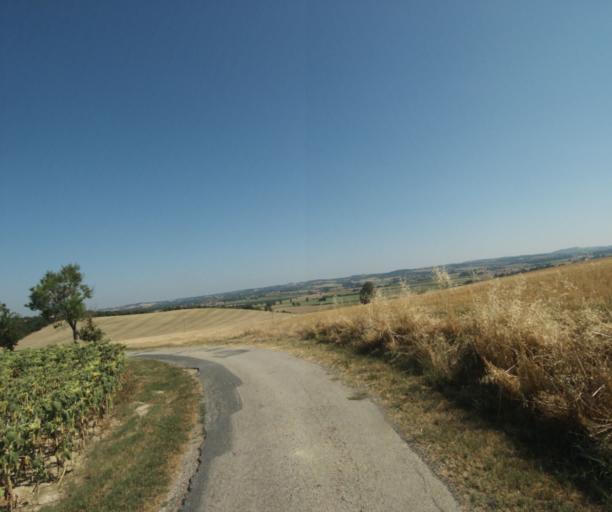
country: FR
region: Midi-Pyrenees
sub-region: Departement de la Haute-Garonne
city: Saint-Felix-Lauragais
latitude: 43.5169
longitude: 1.9401
